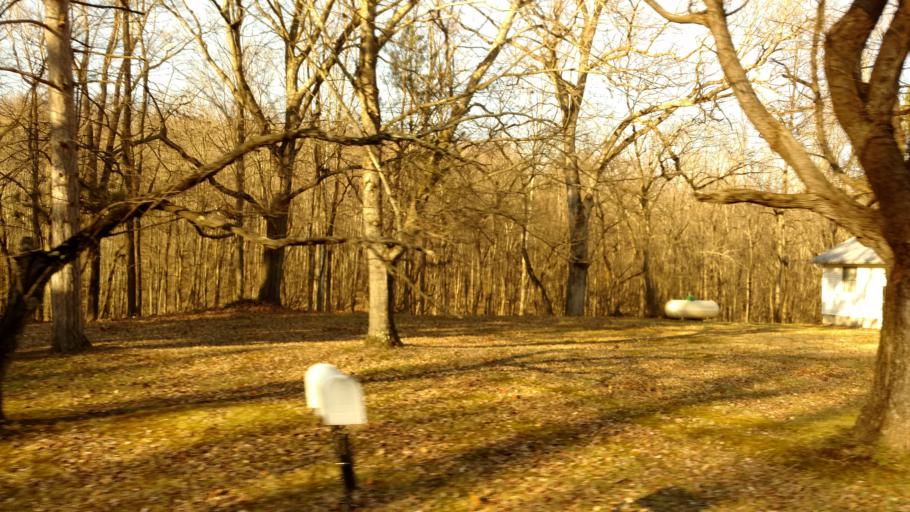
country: US
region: Ohio
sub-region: Richland County
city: Ontario
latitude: 40.7211
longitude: -82.6638
